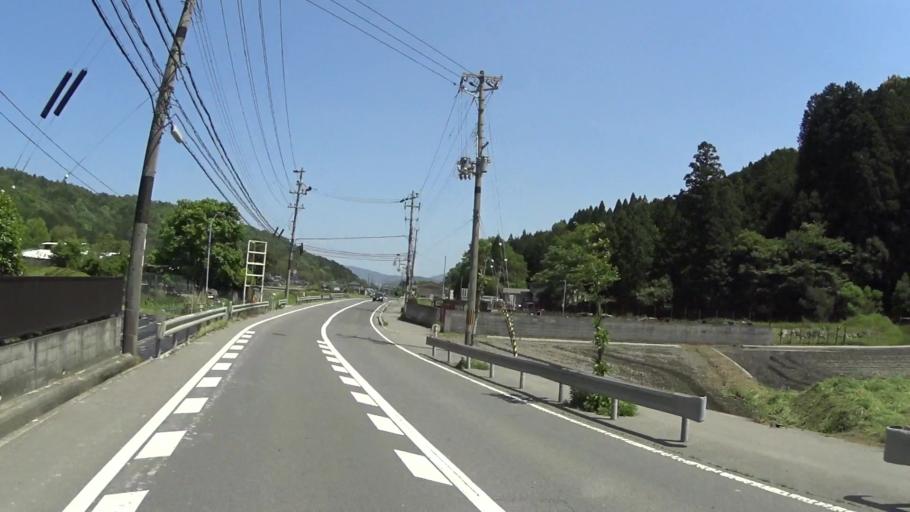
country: JP
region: Kyoto
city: Kameoka
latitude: 35.0262
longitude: 135.5124
